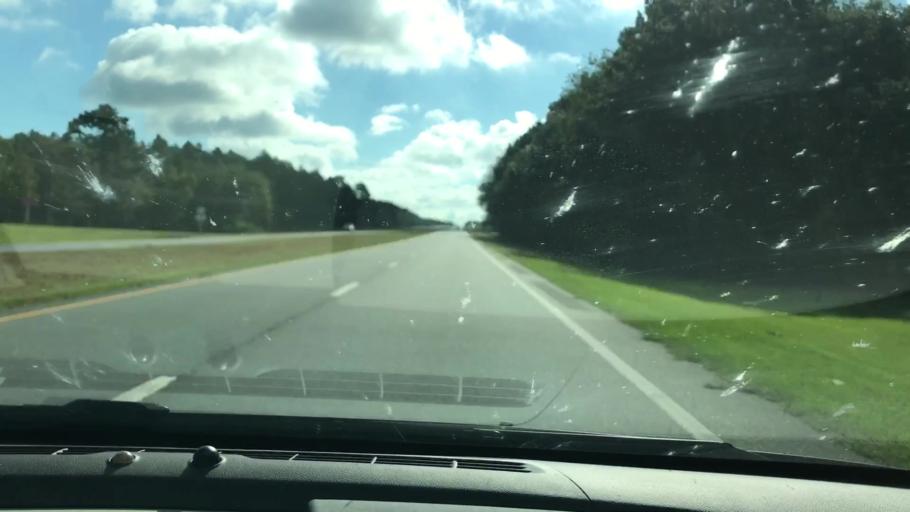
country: US
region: Georgia
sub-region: Worth County
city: Sylvester
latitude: 31.5515
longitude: -83.9368
